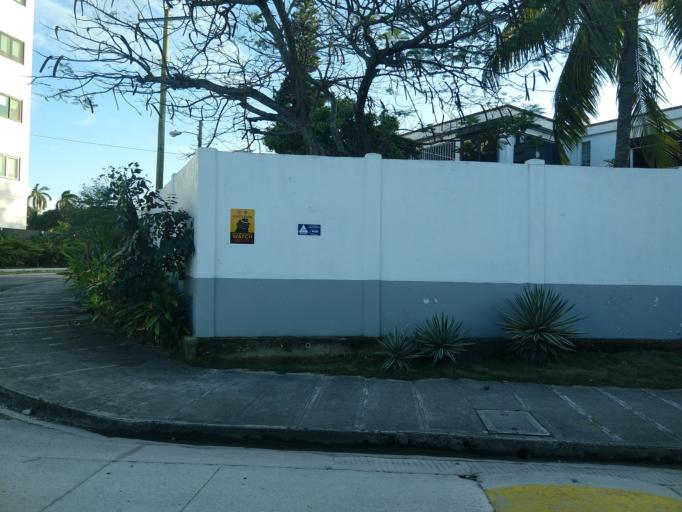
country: BZ
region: Belize
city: Belize City
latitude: 17.5124
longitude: -88.1892
